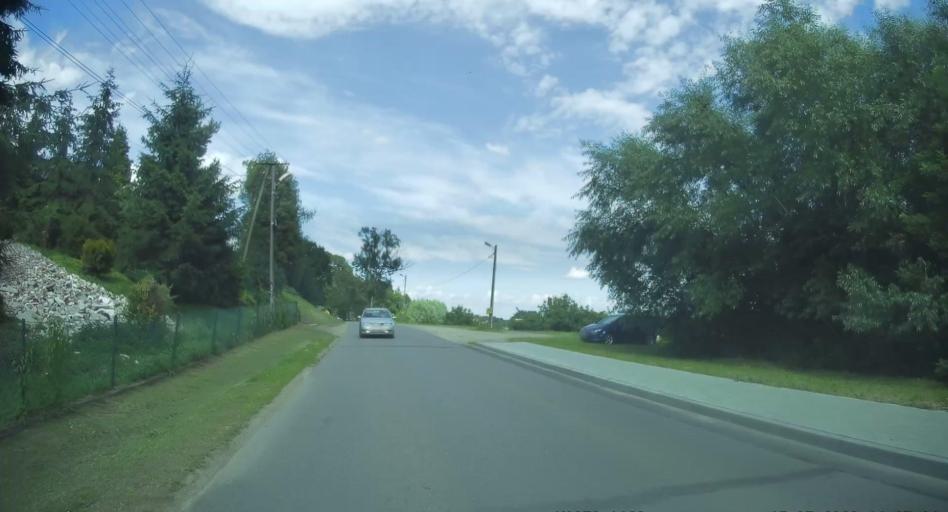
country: PL
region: Subcarpathian Voivodeship
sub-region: Powiat przemyski
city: Medyka
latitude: 49.8144
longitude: 22.8562
